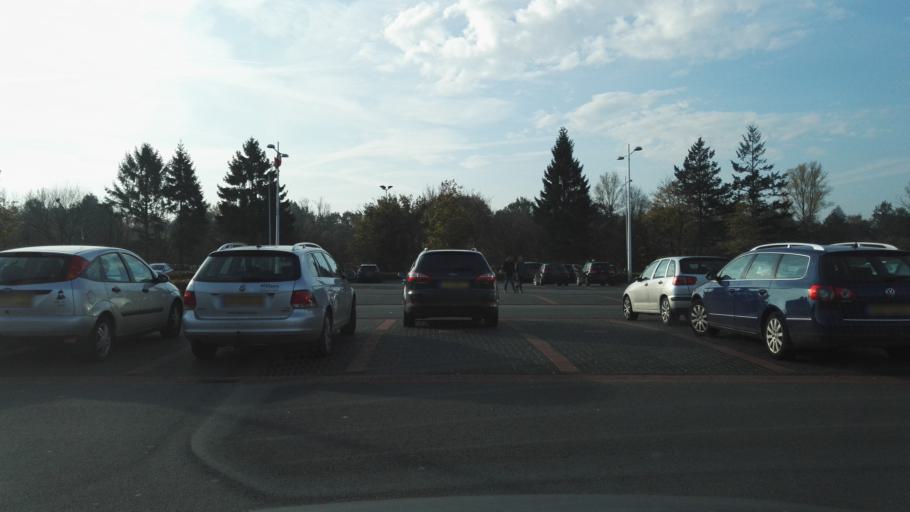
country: NL
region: Gelderland
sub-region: Gemeente Apeldoorn
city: Apeldoorn
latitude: 52.2087
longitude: 5.9961
